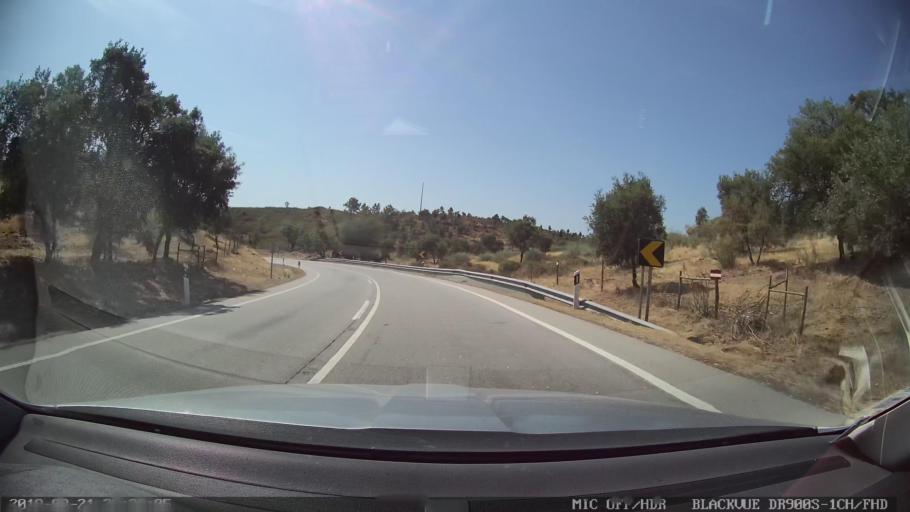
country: PT
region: Guarda
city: Alcains
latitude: 39.8623
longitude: -7.3555
